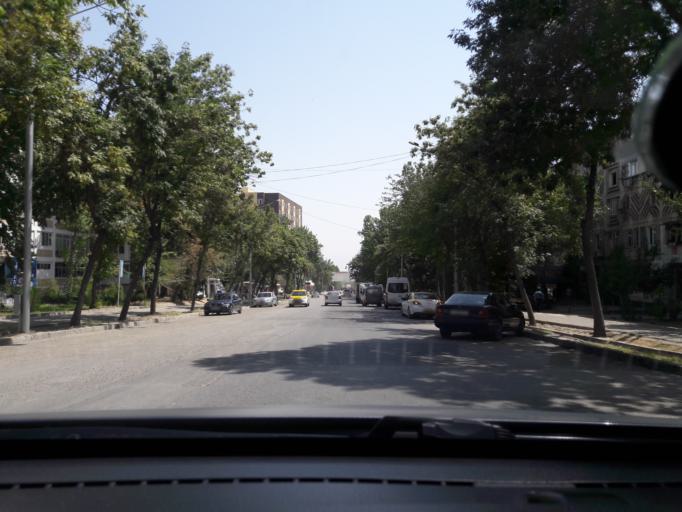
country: TJ
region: Dushanbe
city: Dushanbe
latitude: 38.5891
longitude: 68.7330
